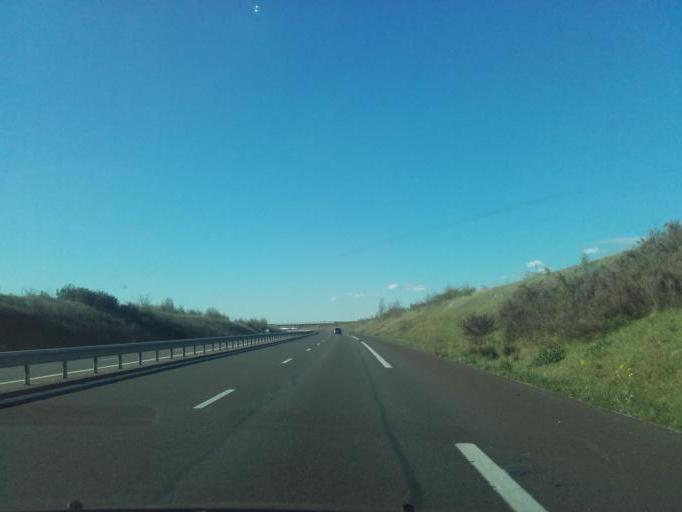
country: FR
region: Rhone-Alpes
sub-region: Departement de l'Isere
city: Janneyrias
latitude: 45.7468
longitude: 5.0954
